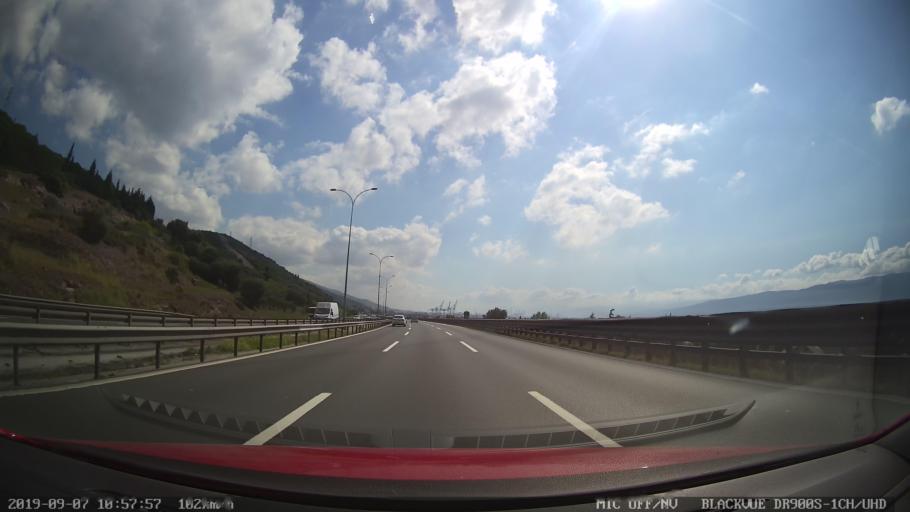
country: TR
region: Kocaeli
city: Hereke
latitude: 40.7790
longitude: 29.6717
